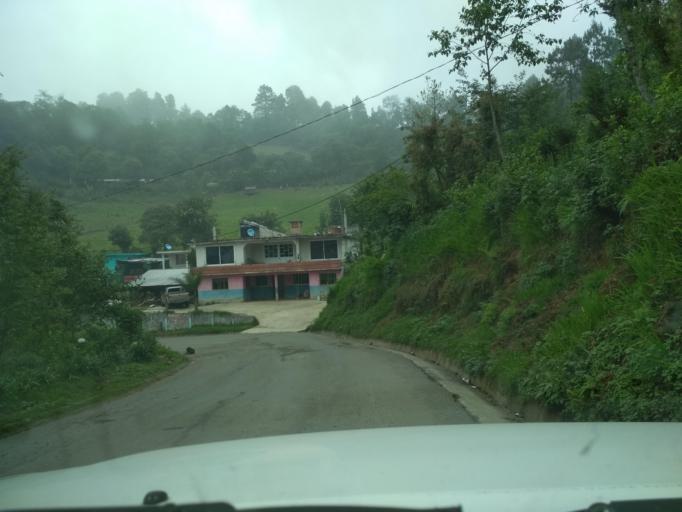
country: MX
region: Veracruz
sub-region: La Perla
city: Chilapa
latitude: 18.9716
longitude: -97.1722
